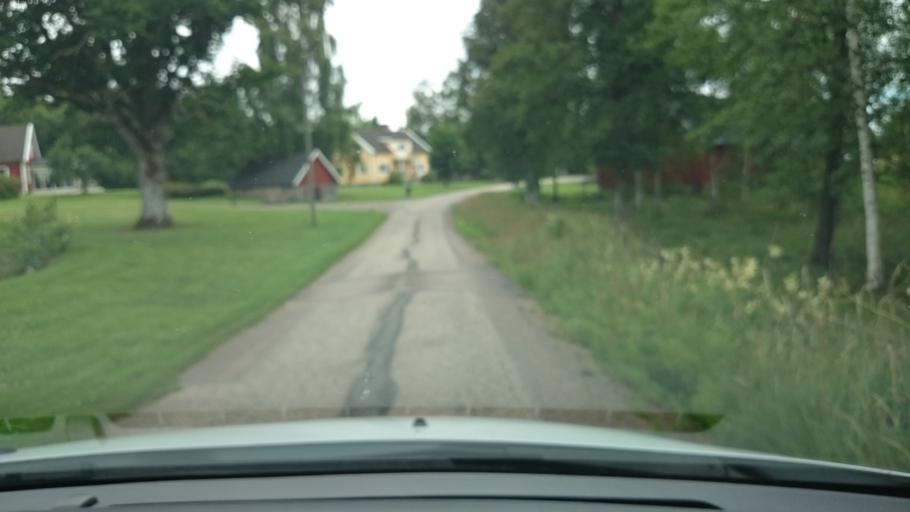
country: SE
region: Halland
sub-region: Hylte Kommun
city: Hyltebruk
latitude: 56.9688
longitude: 13.1980
